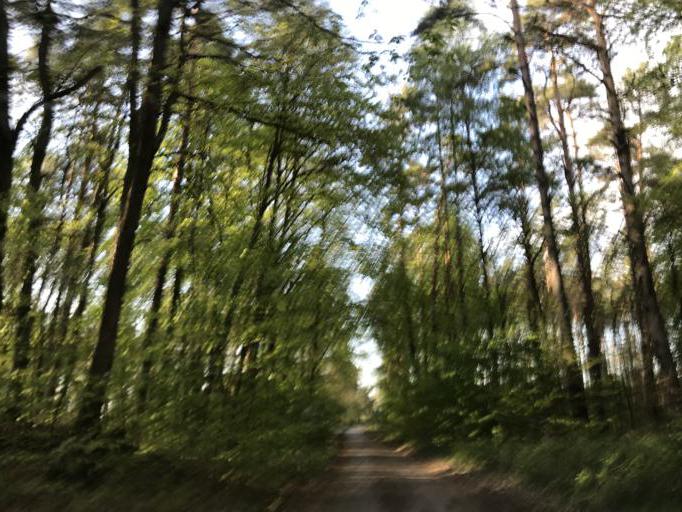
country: DE
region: Brandenburg
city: Joachimsthal
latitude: 52.9705
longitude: 13.7241
